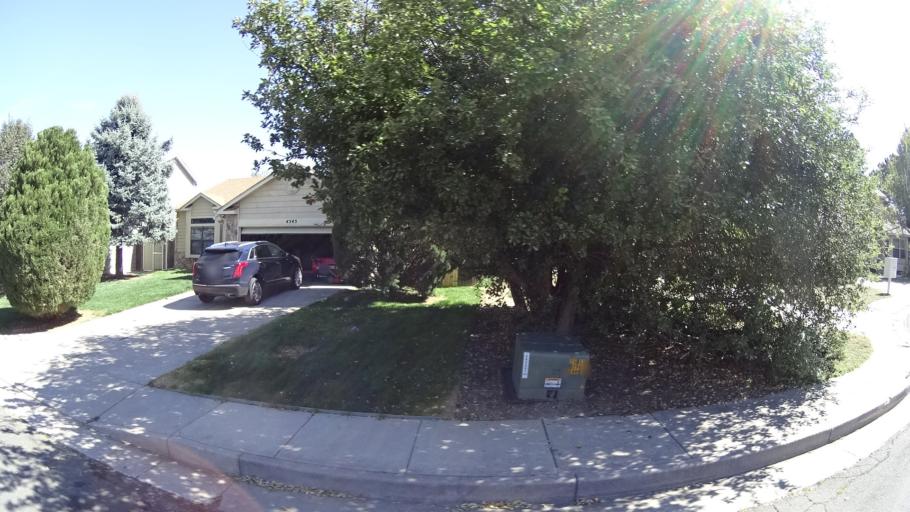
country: US
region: Colorado
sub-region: El Paso County
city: Cimarron Hills
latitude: 38.8976
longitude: -104.7052
